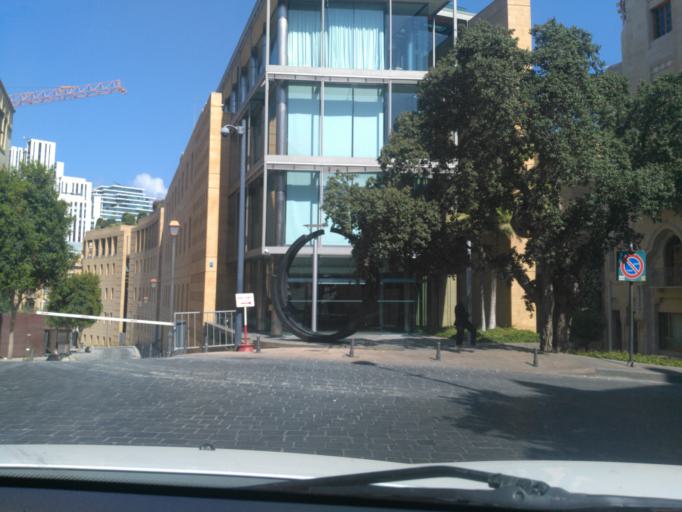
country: LB
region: Beyrouth
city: Beirut
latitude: 33.8980
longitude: 35.5022
